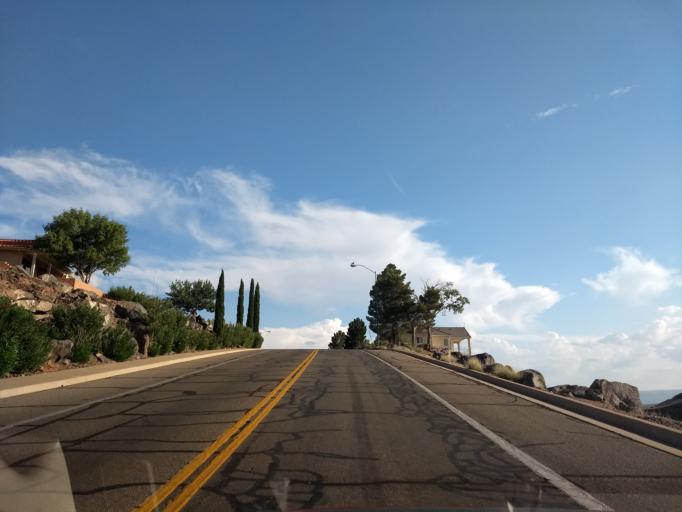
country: US
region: Utah
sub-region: Washington County
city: Saint George
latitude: 37.1120
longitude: -113.5518
